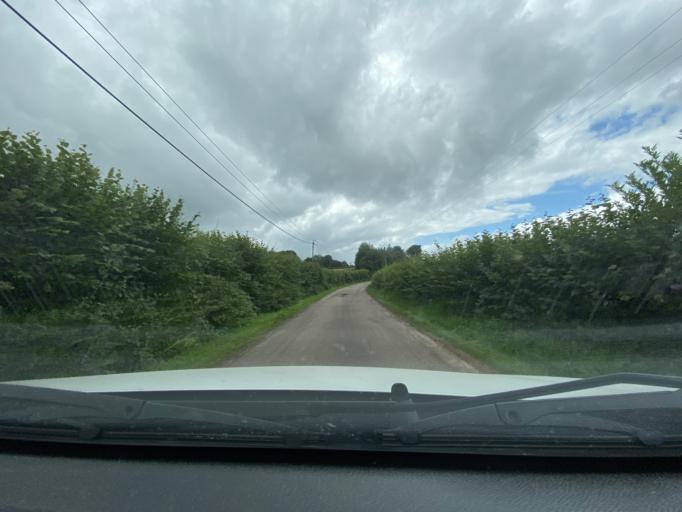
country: FR
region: Bourgogne
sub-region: Departement de la Cote-d'Or
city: Saulieu
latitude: 47.2638
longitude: 4.1961
